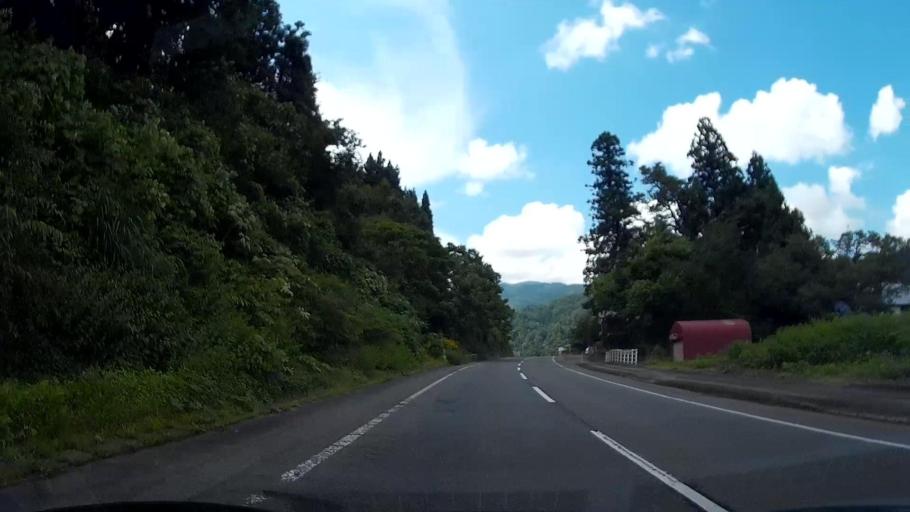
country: JP
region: Niigata
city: Tokamachi
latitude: 36.9938
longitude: 138.6050
